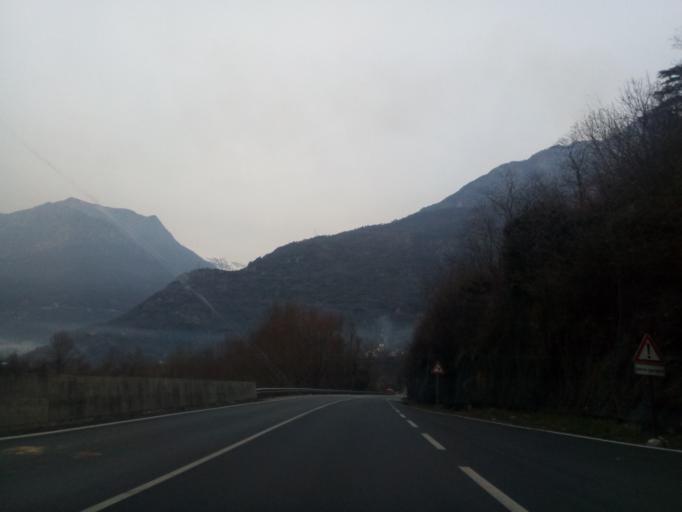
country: IT
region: Piedmont
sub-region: Provincia di Torino
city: Carema
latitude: 45.5756
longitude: 7.8103
